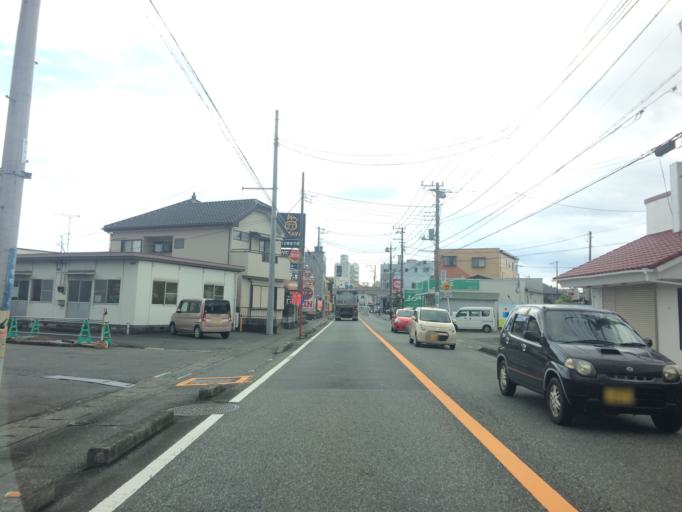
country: JP
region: Shizuoka
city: Fuji
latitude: 35.1607
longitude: 138.6502
